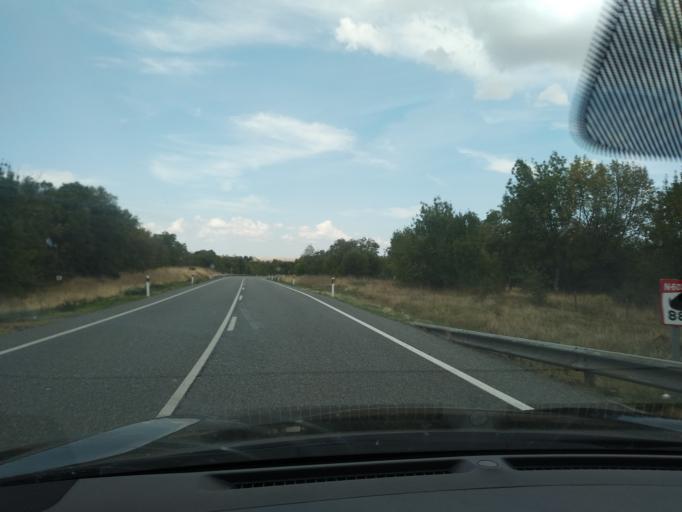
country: ES
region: Castille and Leon
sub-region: Provincia de Segovia
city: Palazuelos de Eresma
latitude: 40.8788
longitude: -4.0985
